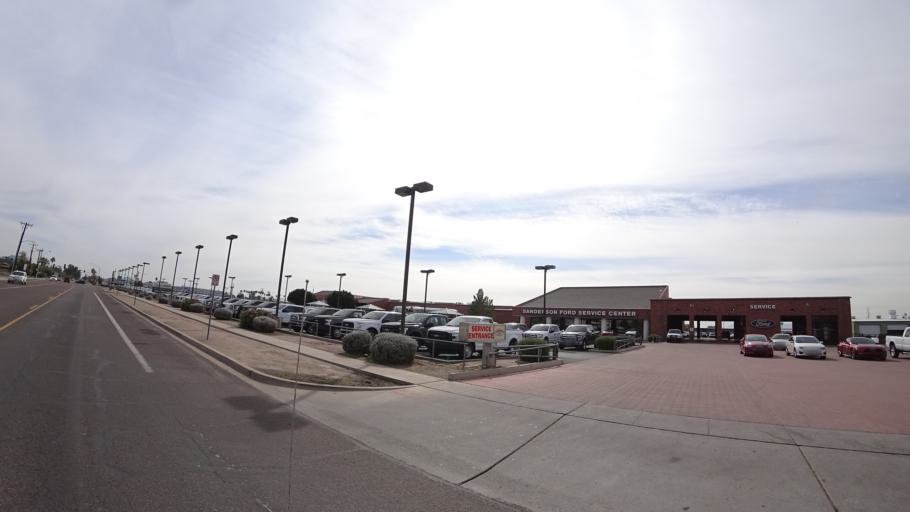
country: US
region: Arizona
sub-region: Maricopa County
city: Glendale
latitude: 33.5312
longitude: -112.1711
